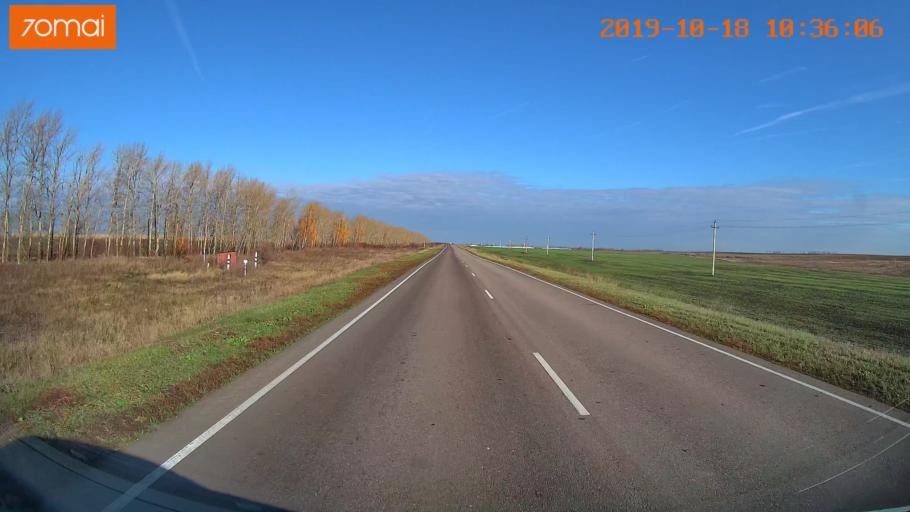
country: RU
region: Tula
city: Kurkino
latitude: 53.5430
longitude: 38.6236
